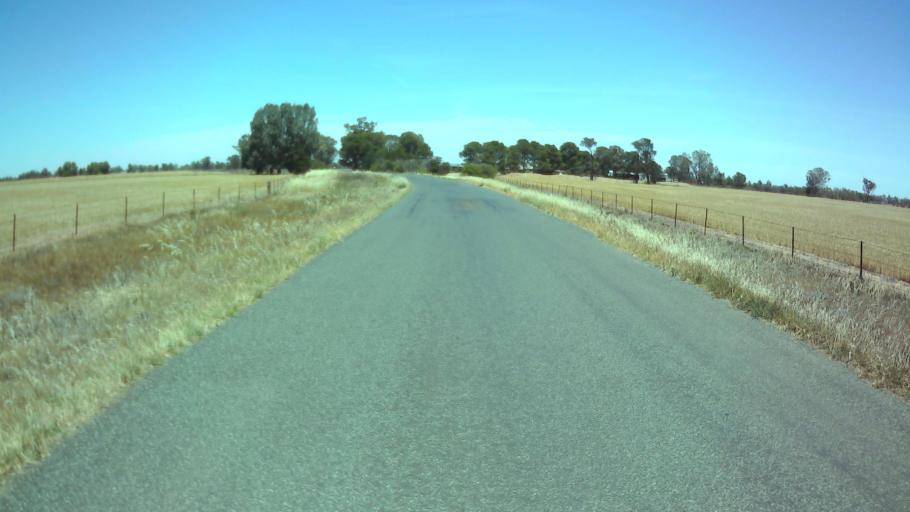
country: AU
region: New South Wales
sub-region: Weddin
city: Grenfell
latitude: -34.0447
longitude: 147.7844
